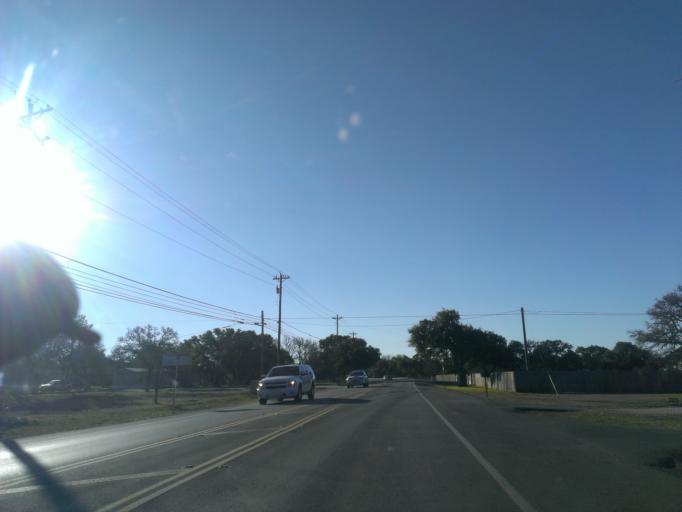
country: US
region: Texas
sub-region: Hays County
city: Dripping Springs
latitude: 30.1852
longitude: -98.0865
